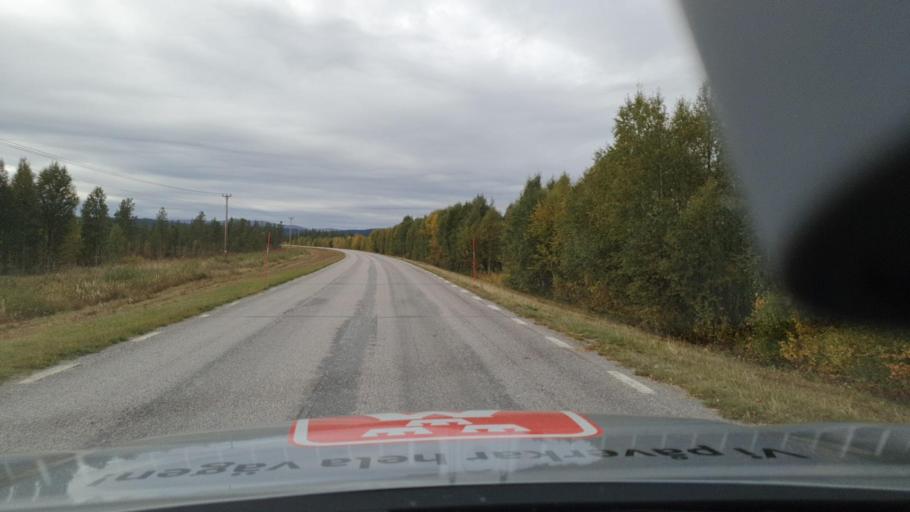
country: SE
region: Norrbotten
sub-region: Arjeplogs Kommun
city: Arjeplog
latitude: 66.1337
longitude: 17.3559
